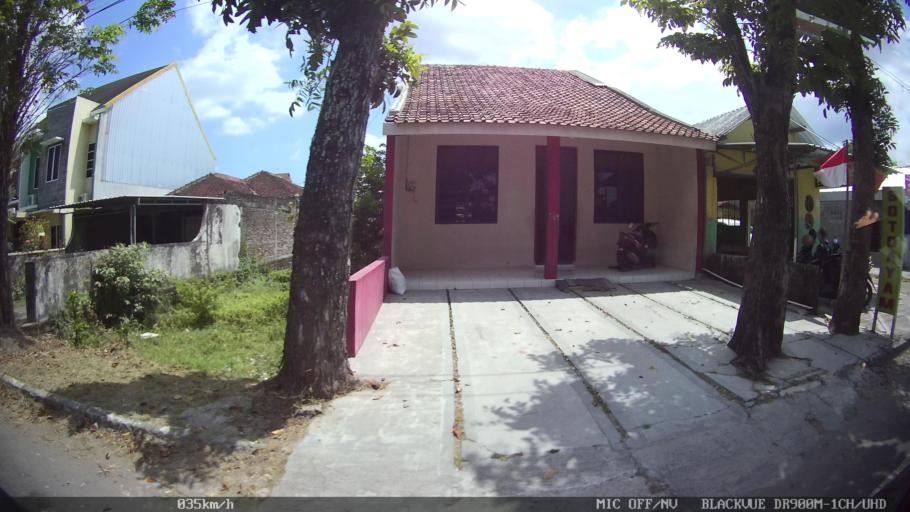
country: ID
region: Daerah Istimewa Yogyakarta
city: Bantul
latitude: -7.8905
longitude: 110.3334
